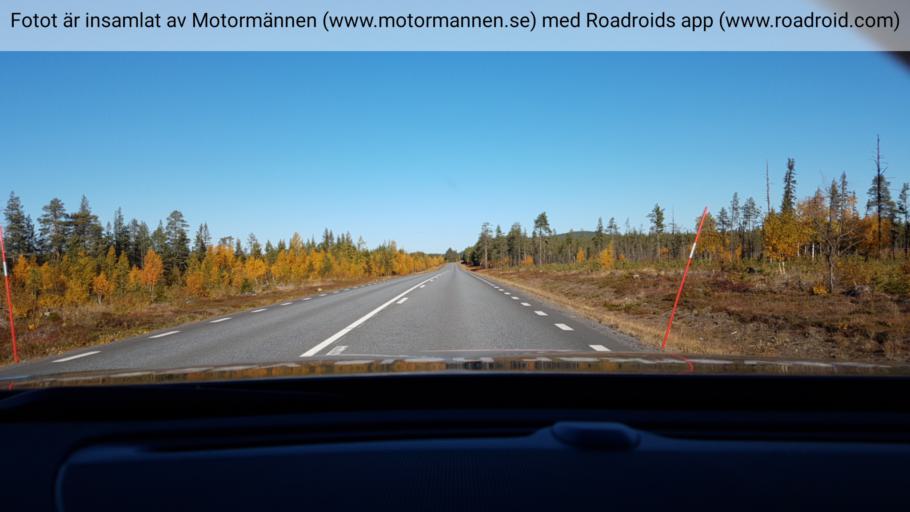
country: SE
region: Norrbotten
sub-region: Arvidsjaurs Kommun
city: Arvidsjaur
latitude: 65.5012
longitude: 19.2963
